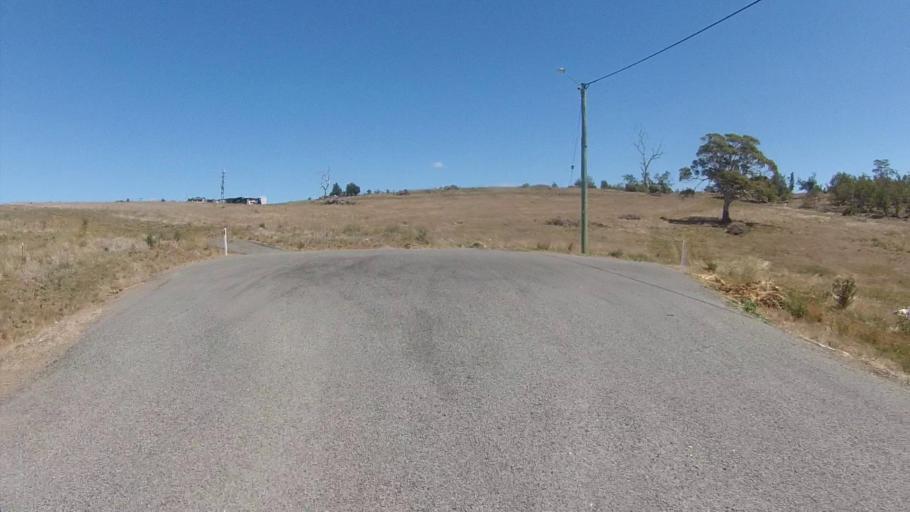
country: AU
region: Tasmania
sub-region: Sorell
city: Sorell
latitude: -42.7590
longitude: 147.5578
